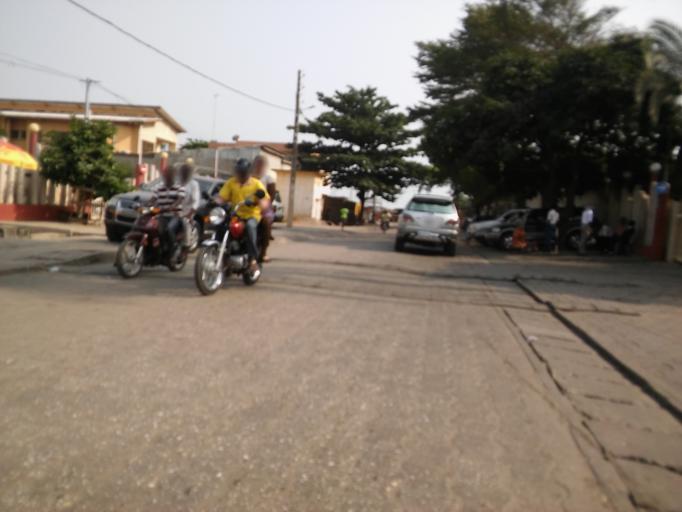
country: BJ
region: Littoral
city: Cotonou
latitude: 6.3594
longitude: 2.4452
